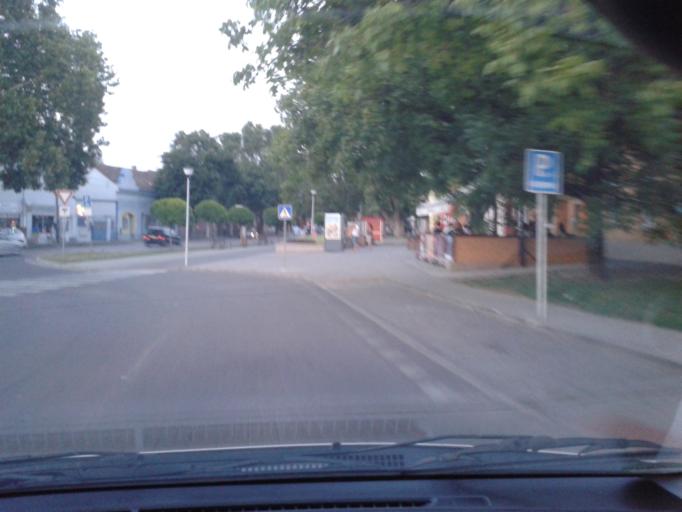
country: SK
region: Nitriansky
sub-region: Okres Nove Zamky
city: Sturovo
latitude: 47.7989
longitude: 18.7177
